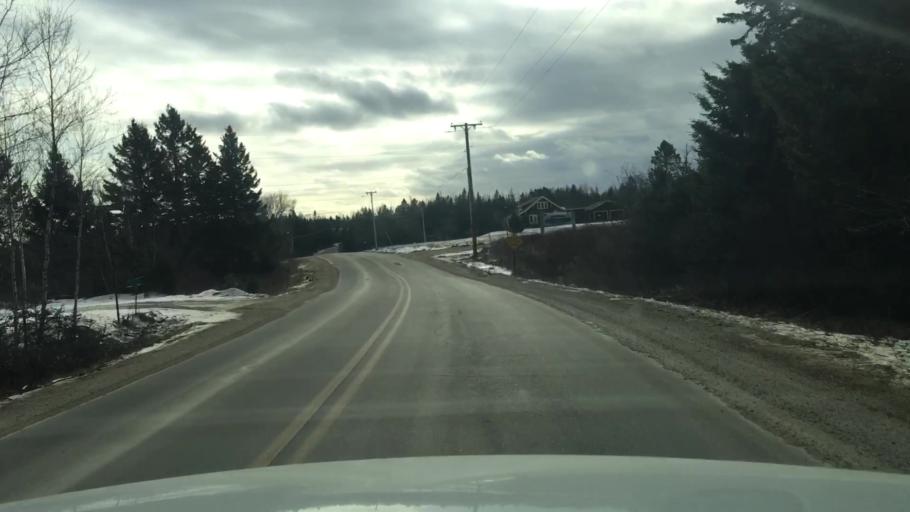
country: US
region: Maine
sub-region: Washington County
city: Jonesport
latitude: 44.6311
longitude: -67.5957
